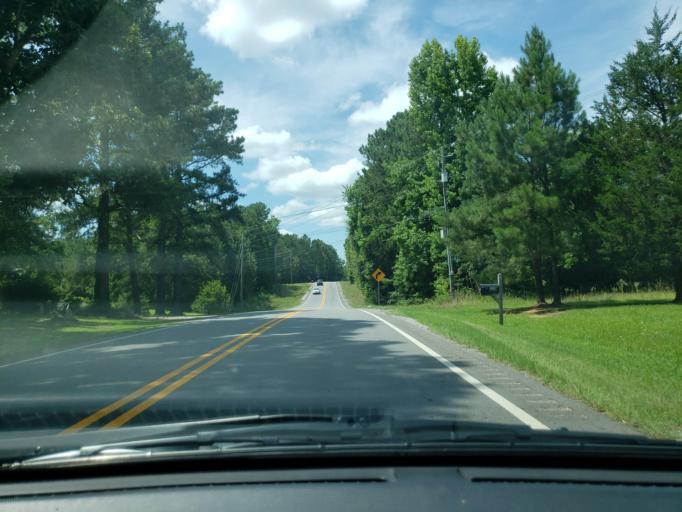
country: US
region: Alabama
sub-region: Elmore County
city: Eclectic
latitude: 32.6311
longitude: -85.9526
